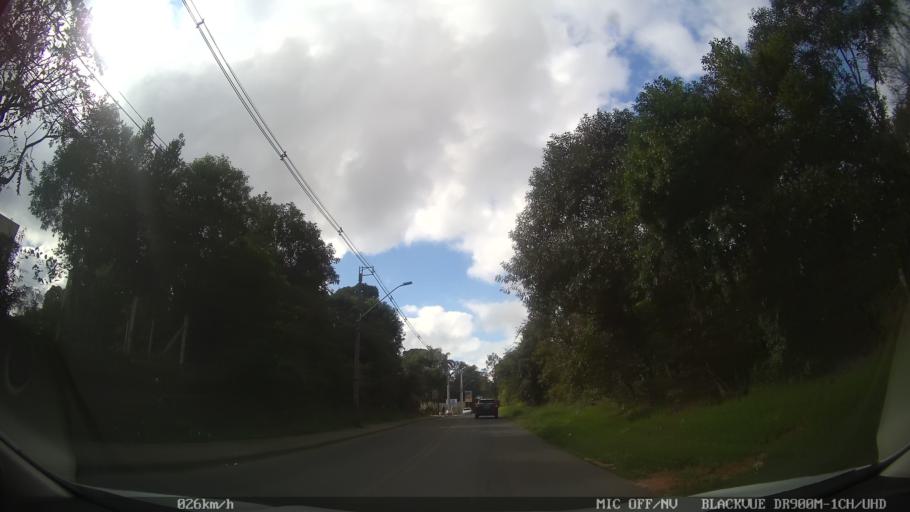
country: BR
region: Parana
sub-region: Colombo
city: Colombo
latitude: -25.3484
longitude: -49.2037
